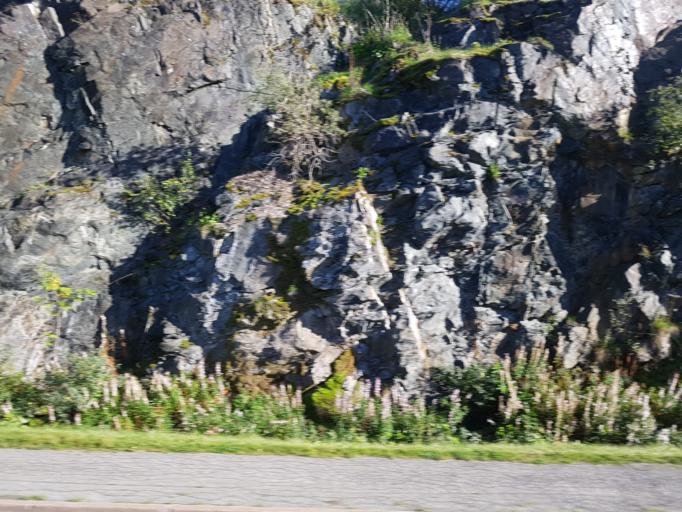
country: NO
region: Sor-Trondelag
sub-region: Skaun
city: Borsa
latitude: 63.4481
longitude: 10.1927
